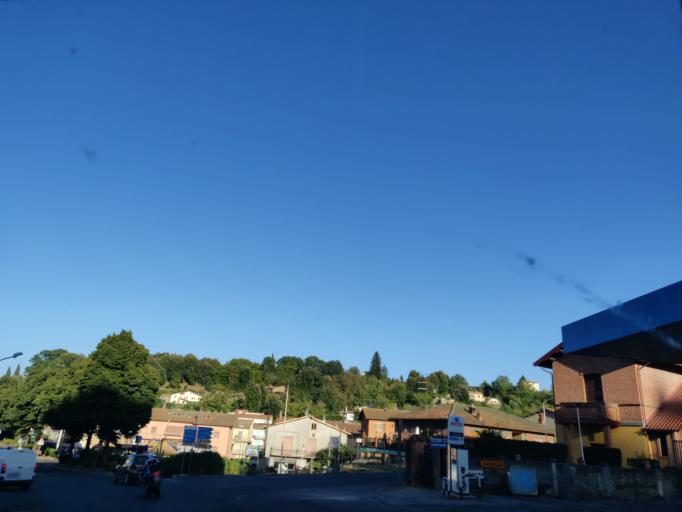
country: IT
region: Latium
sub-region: Provincia di Viterbo
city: Acquapendente
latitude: 42.7413
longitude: 11.8648
